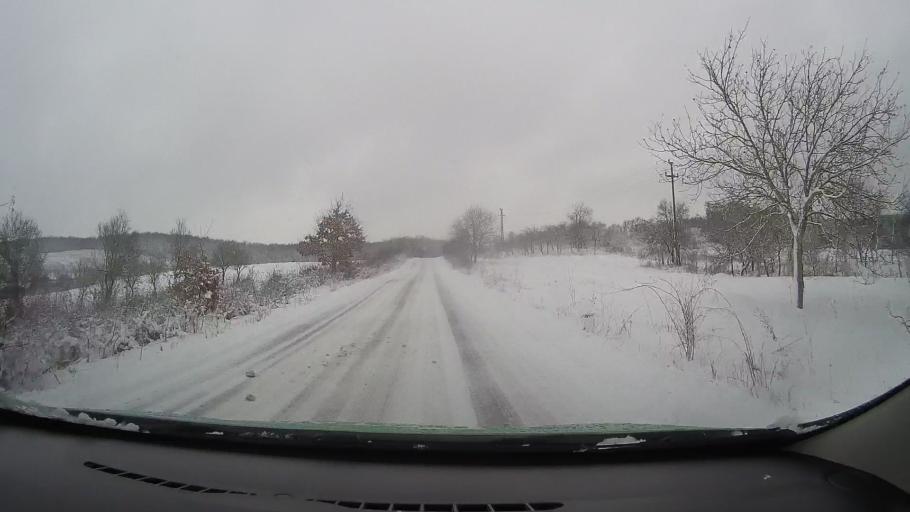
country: RO
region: Hunedoara
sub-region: Comuna Pestisu Mic
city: Pestisu Mic
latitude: 45.8159
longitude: 22.8951
